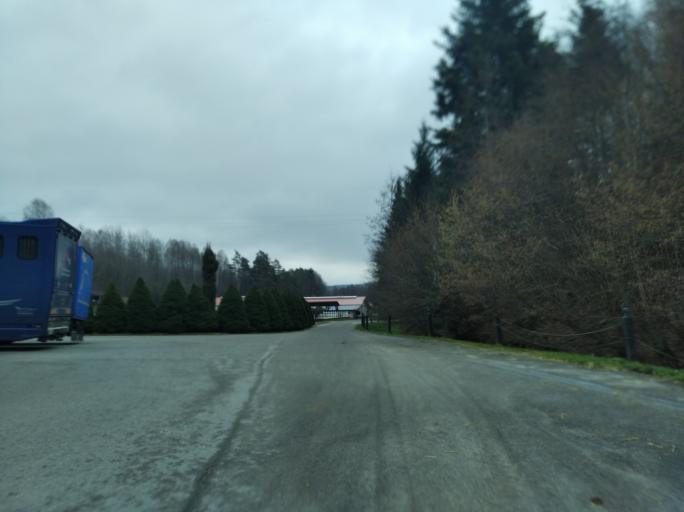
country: PL
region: Subcarpathian Voivodeship
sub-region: Powiat strzyzowski
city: Strzyzow
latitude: 49.8944
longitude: 21.8076
